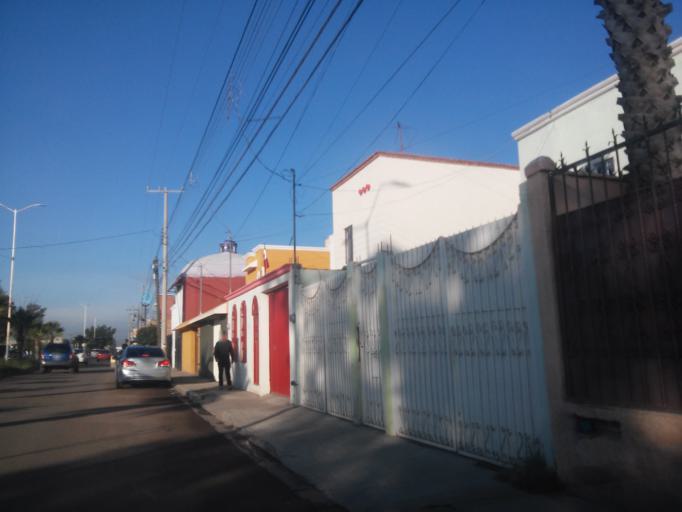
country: MX
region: Durango
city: Victoria de Durango
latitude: 24.0482
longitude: -104.6139
